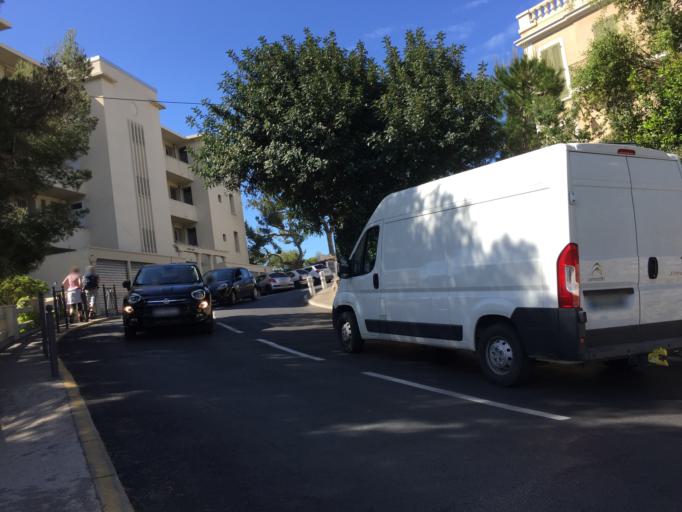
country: FR
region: Provence-Alpes-Cote d'Azur
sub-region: Departement des Bouches-du-Rhone
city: Cassis
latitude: 43.2124
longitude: 5.5308
